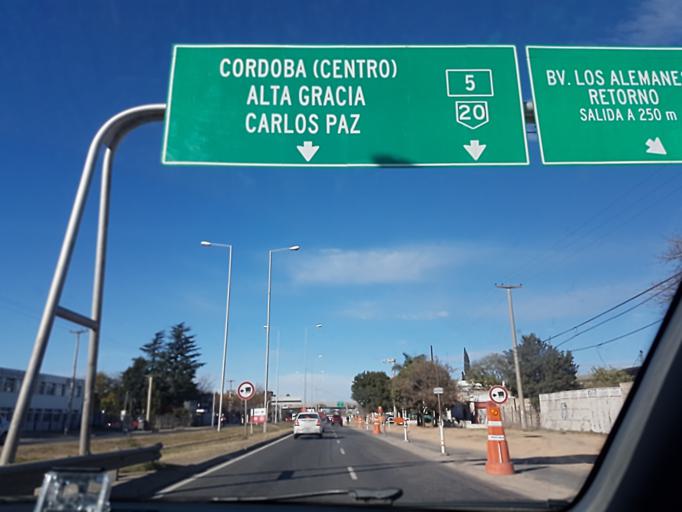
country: AR
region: Cordoba
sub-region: Departamento de Capital
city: Cordoba
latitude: -31.3380
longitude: -64.2079
